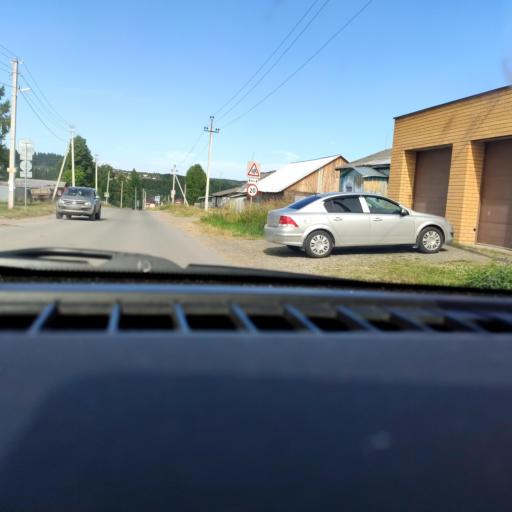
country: RU
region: Perm
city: Polazna
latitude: 58.3433
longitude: 56.2405
